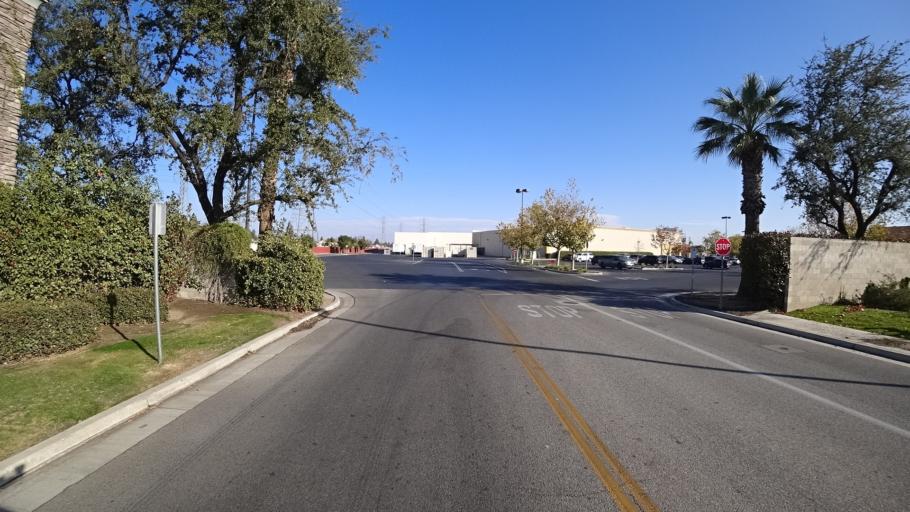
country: US
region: California
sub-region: Kern County
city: Greenacres
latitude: 35.3862
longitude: -119.1076
